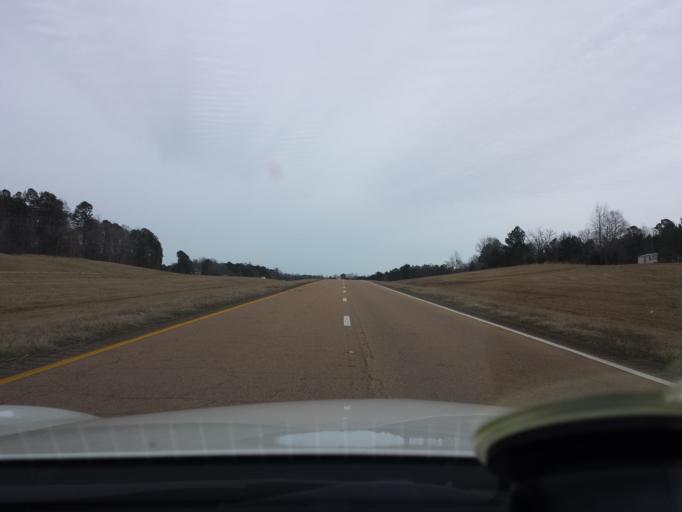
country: US
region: Mississippi
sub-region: Neshoba County
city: Pearl River
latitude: 32.9841
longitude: -89.2353
